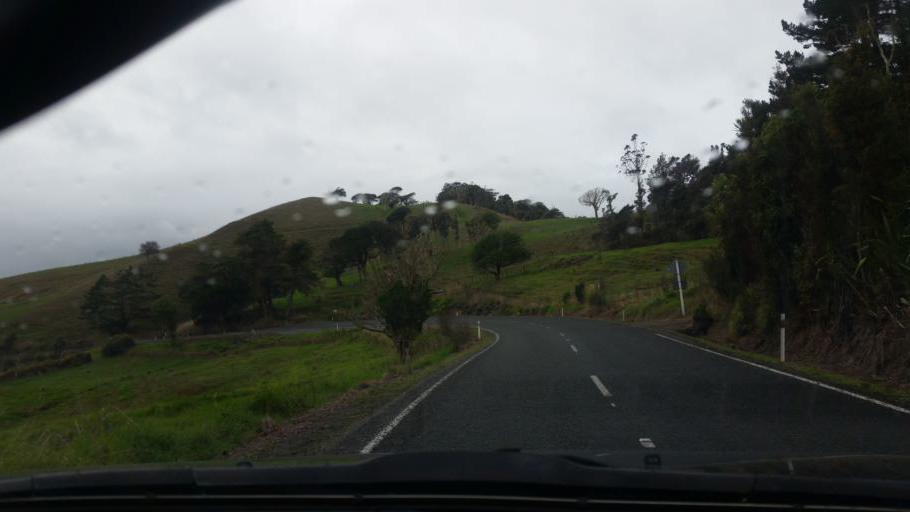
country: NZ
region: Northland
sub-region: Kaipara District
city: Dargaville
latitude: -36.0145
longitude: 173.9795
